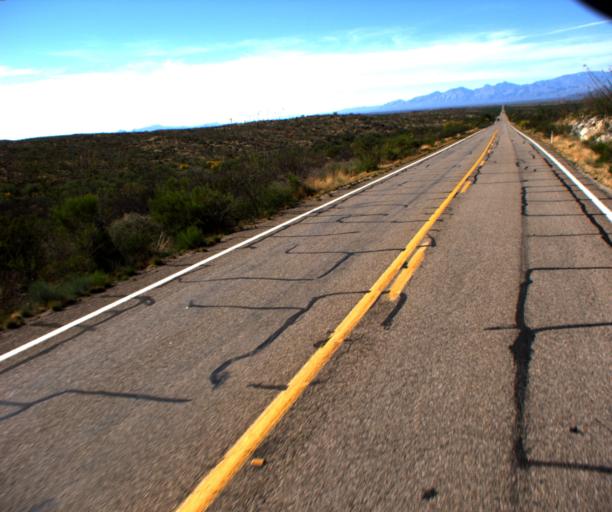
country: US
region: Arizona
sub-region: Pima County
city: Corona de Tucson
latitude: 31.9317
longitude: -110.6591
